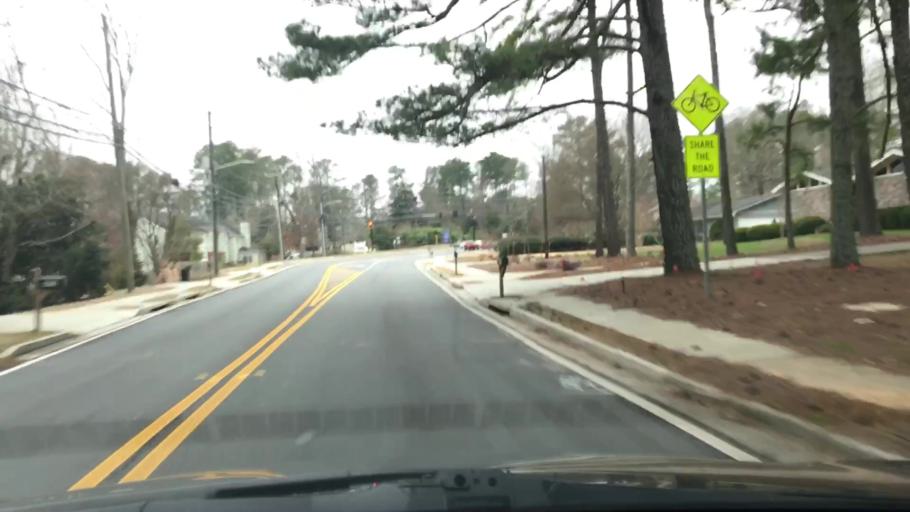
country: US
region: Georgia
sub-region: DeKalb County
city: Doraville
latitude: 33.9365
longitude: -84.2919
